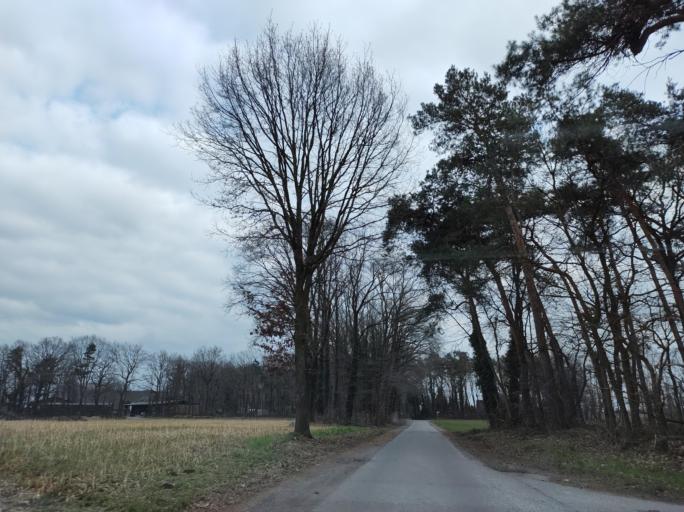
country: DE
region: North Rhine-Westphalia
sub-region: Regierungsbezirk Detmold
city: Delbruck
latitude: 51.7400
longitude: 8.5726
